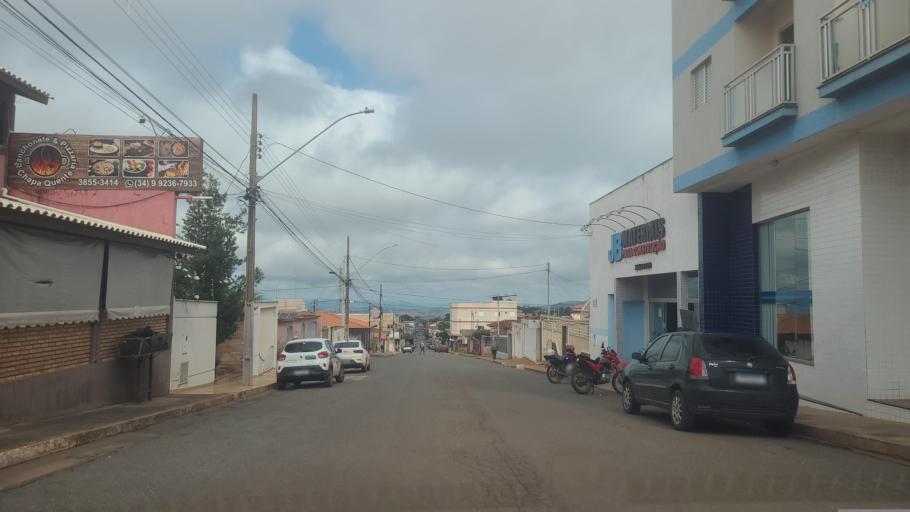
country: BR
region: Minas Gerais
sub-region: Carmo Do Paranaiba
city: Carmo do Paranaiba
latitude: -19.1955
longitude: -46.2402
